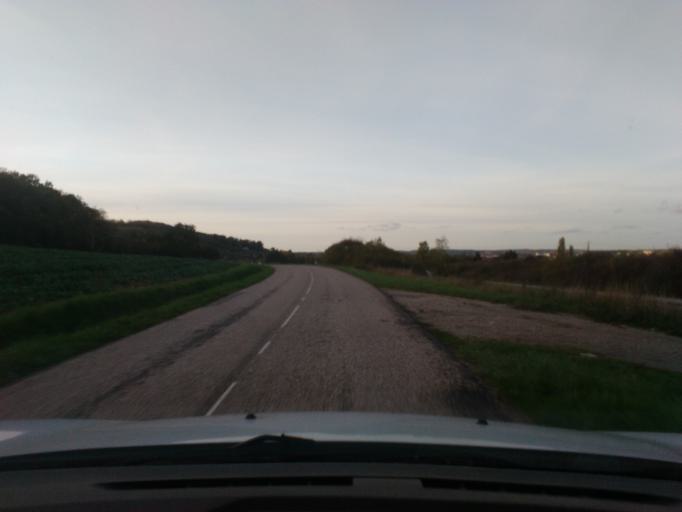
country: FR
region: Lorraine
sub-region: Departement des Vosges
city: Charmes
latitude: 48.3513
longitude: 6.3005
